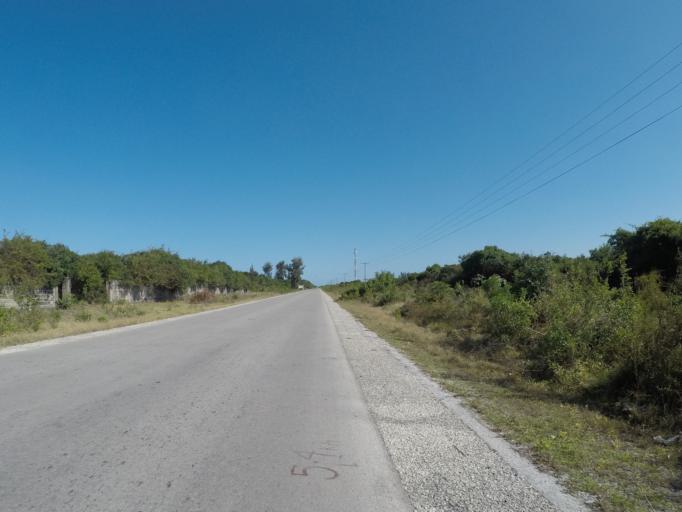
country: TZ
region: Zanzibar Central/South
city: Nganane
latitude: -6.1742
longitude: 39.5268
